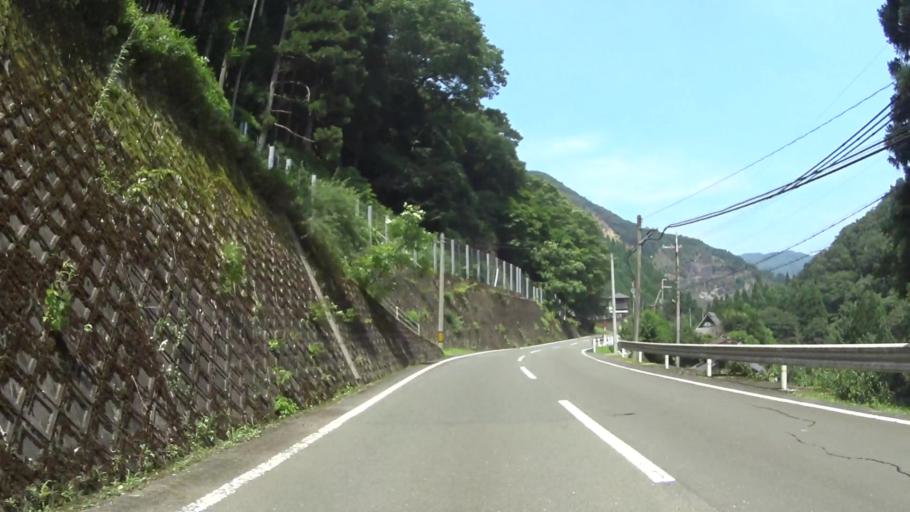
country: JP
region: Kyoto
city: Ayabe
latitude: 35.2863
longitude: 135.4275
